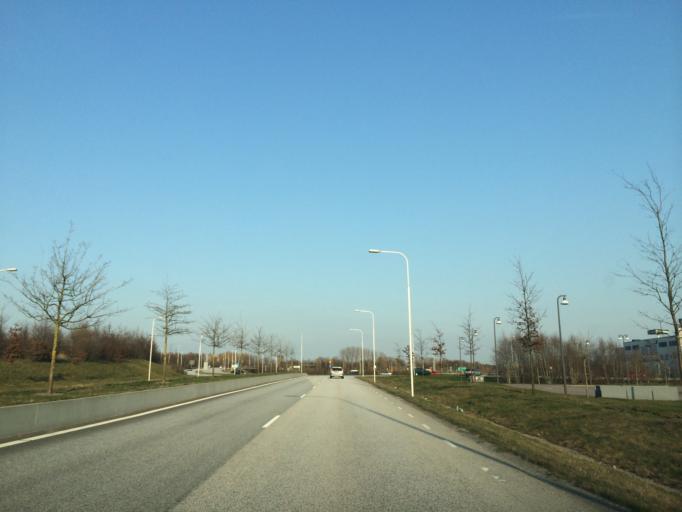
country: SE
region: Skane
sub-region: Malmo
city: Tygelsjo
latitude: 55.5540
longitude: 12.9930
